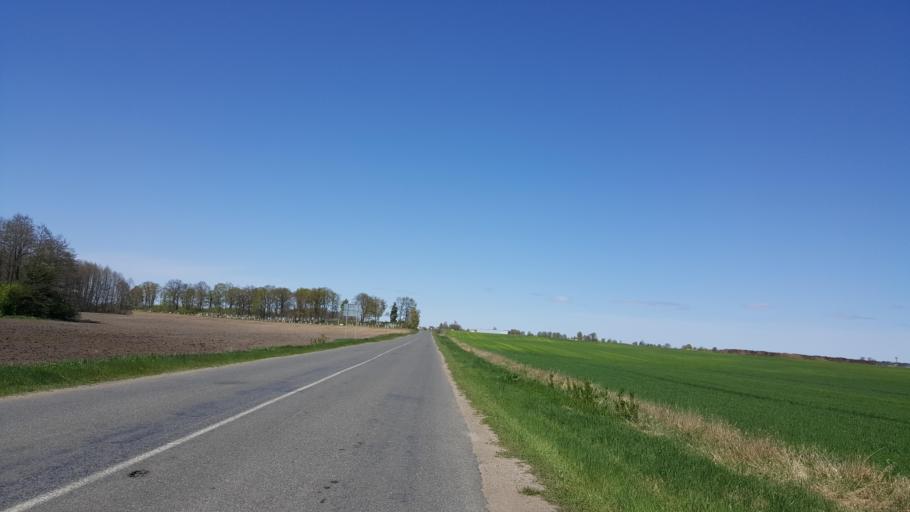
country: BY
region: Brest
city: Charnawchytsy
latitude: 52.3278
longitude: 23.6075
